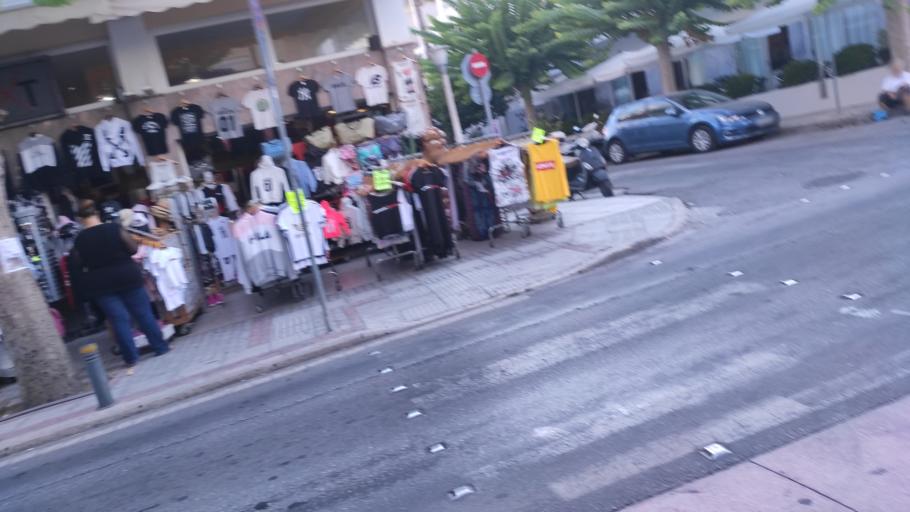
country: GR
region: South Aegean
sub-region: Nomos Dodekanisou
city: Kos
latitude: 36.8978
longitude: 27.2848
